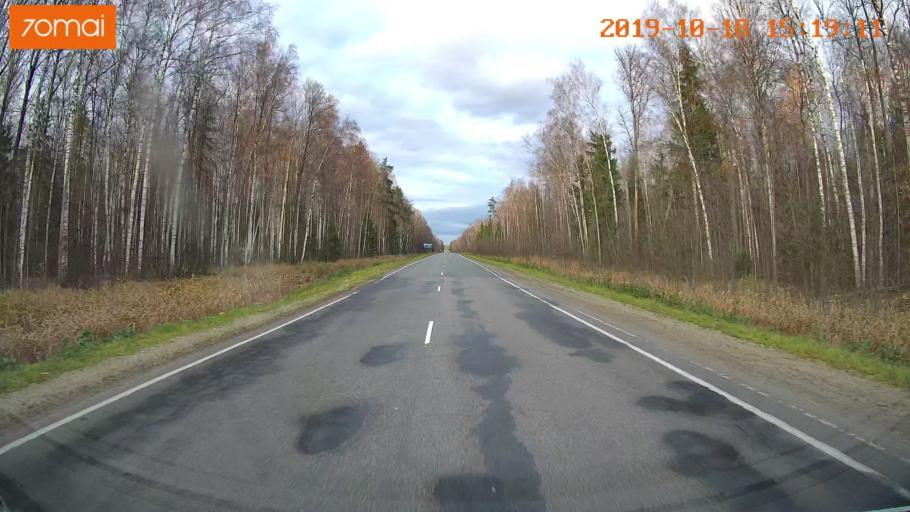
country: RU
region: Vladimir
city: Anopino
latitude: 55.6693
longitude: 40.7358
